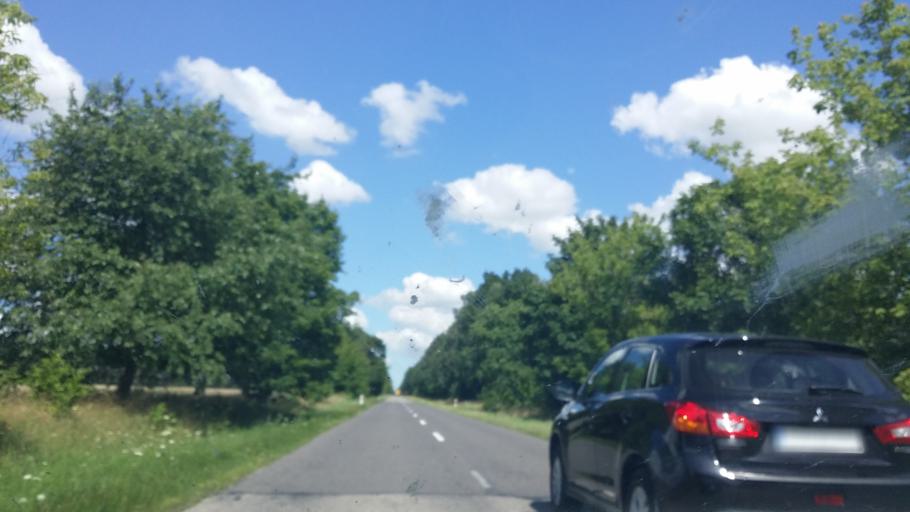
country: PL
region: West Pomeranian Voivodeship
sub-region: Powiat swidwinski
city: Slawoborze
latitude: 53.9173
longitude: 15.6869
